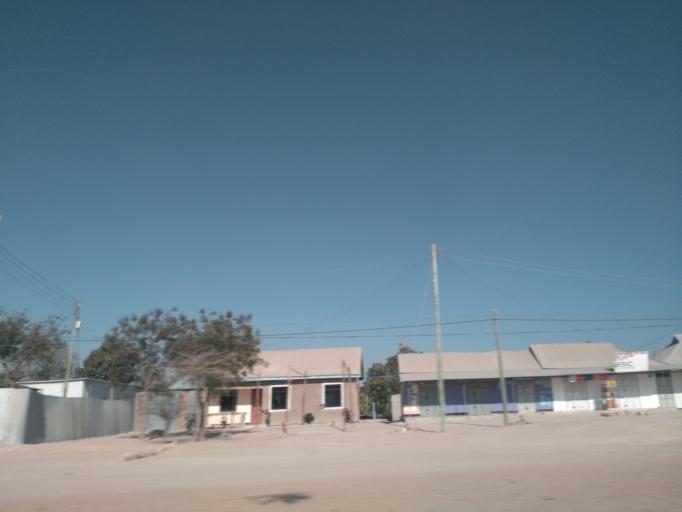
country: TZ
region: Dodoma
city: Dodoma
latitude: -6.1114
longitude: 35.7479
